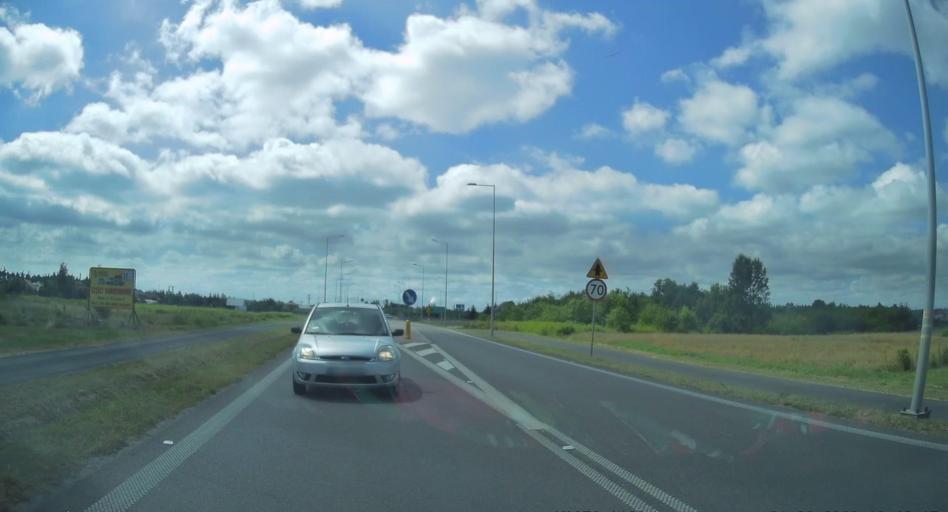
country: PL
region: Subcarpathian Voivodeship
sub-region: Powiat mielecki
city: Mielec
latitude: 50.3313
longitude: 21.4881
